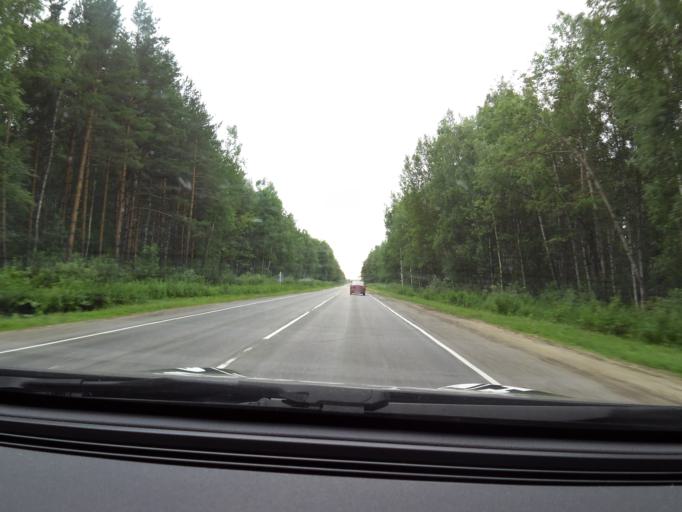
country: RU
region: Vladimir
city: Vorsha
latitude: 56.0858
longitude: 40.1006
